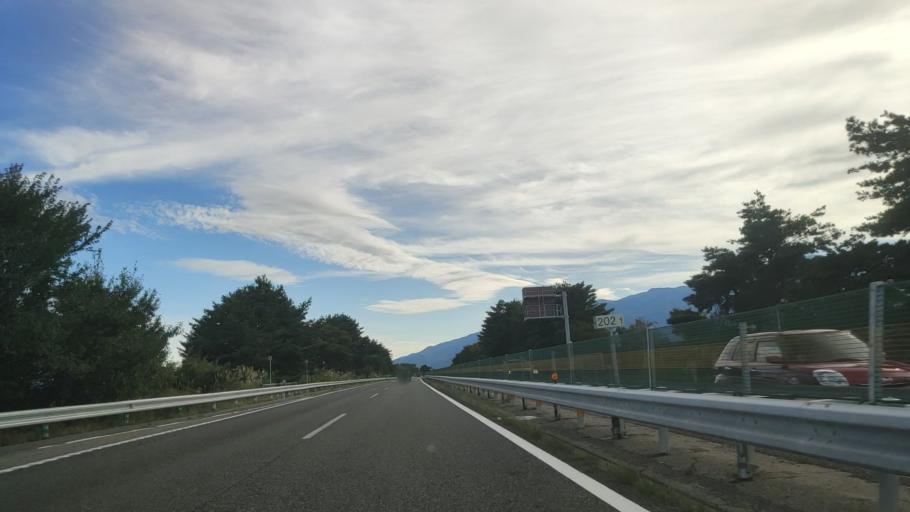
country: JP
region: Nagano
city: Ina
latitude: 35.8929
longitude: 137.9598
